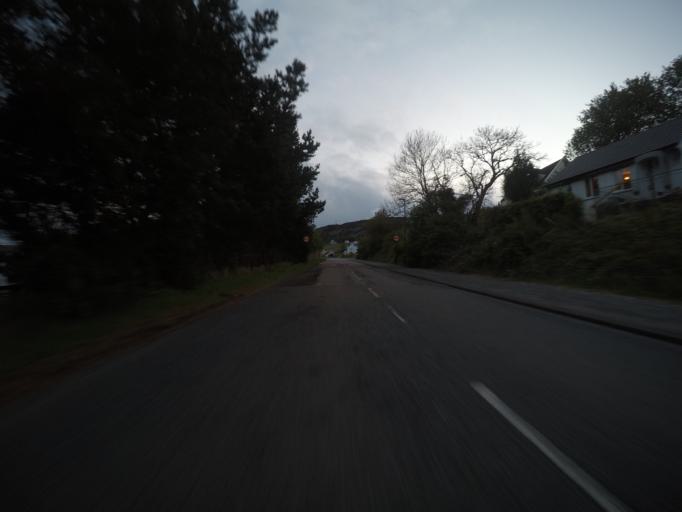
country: GB
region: Scotland
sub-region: Highland
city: Portree
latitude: 57.5912
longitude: -6.3656
